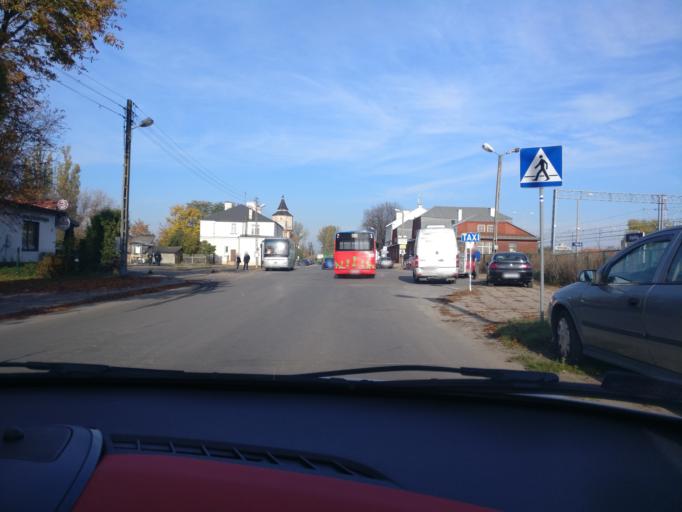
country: PL
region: Lublin Voivodeship
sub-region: Powiat rycki
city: Deblin
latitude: 51.5768
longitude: 21.8356
